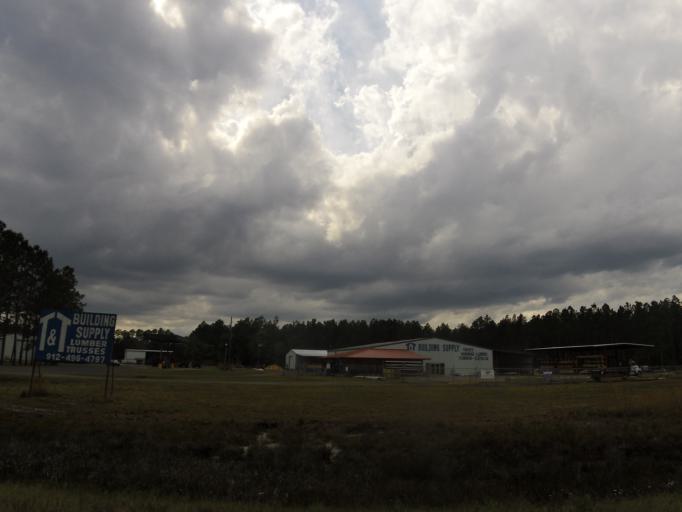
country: US
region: Georgia
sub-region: Charlton County
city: Folkston
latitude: 30.8763
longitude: -82.0148
